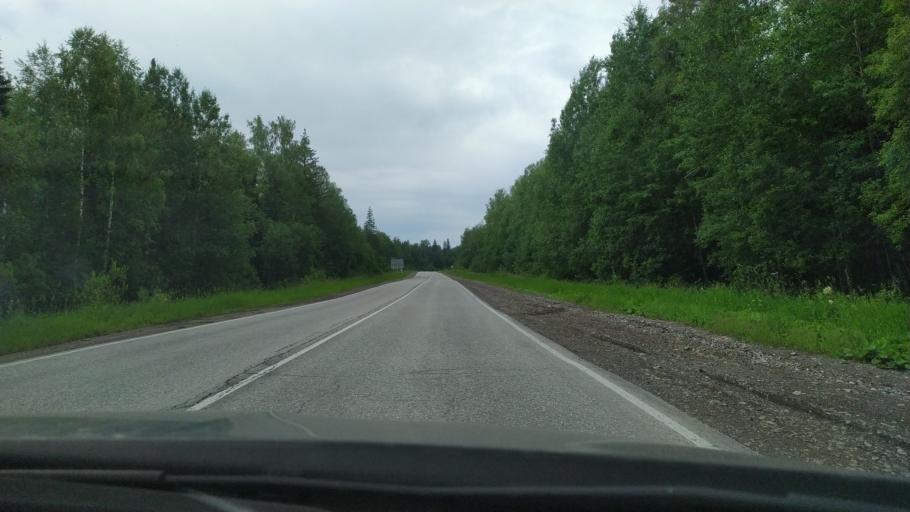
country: RU
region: Perm
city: Gremyachinsk
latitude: 58.4356
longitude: 57.8843
